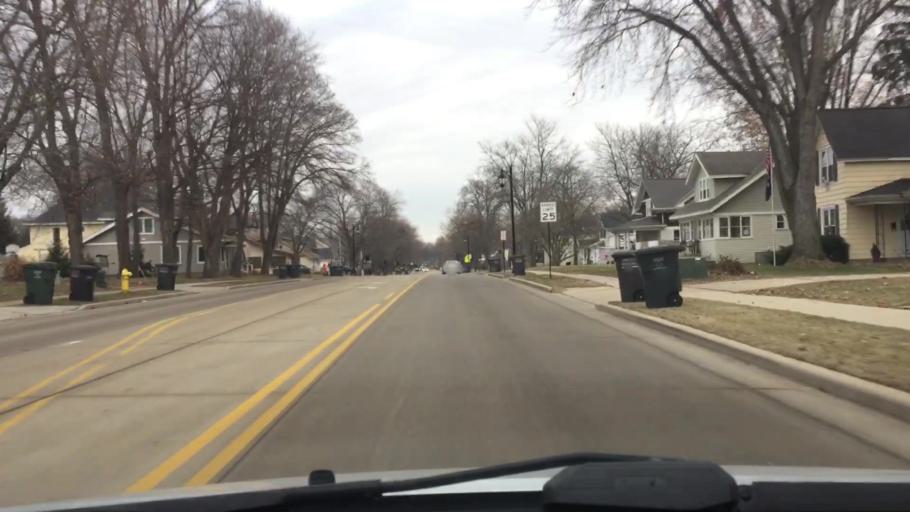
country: US
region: Wisconsin
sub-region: Waukesha County
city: Oconomowoc
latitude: 43.1163
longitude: -88.5158
